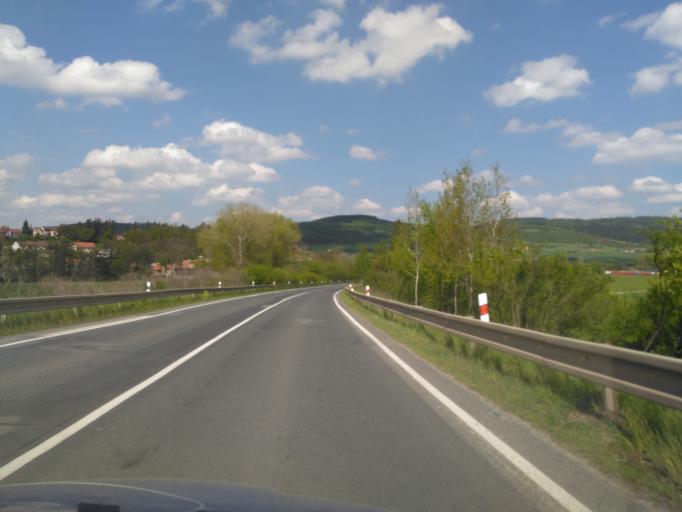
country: CZ
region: Central Bohemia
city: Zdice
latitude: 49.8934
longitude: 13.9665
